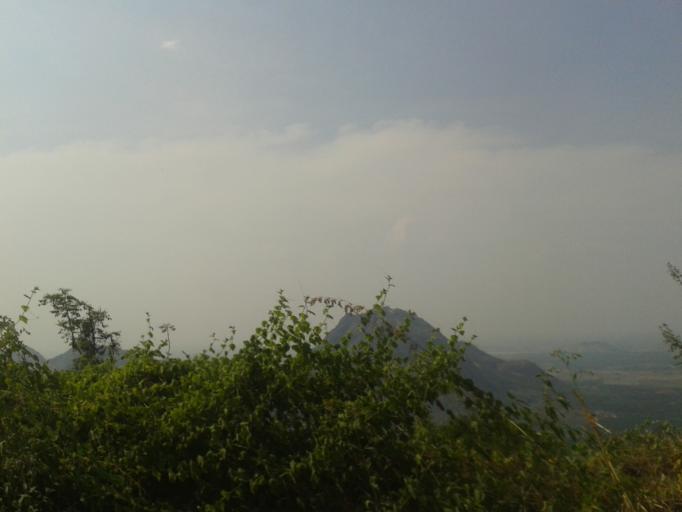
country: IN
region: Tamil Nadu
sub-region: Dindigul
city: Palani
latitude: 10.3598
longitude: 77.5249
